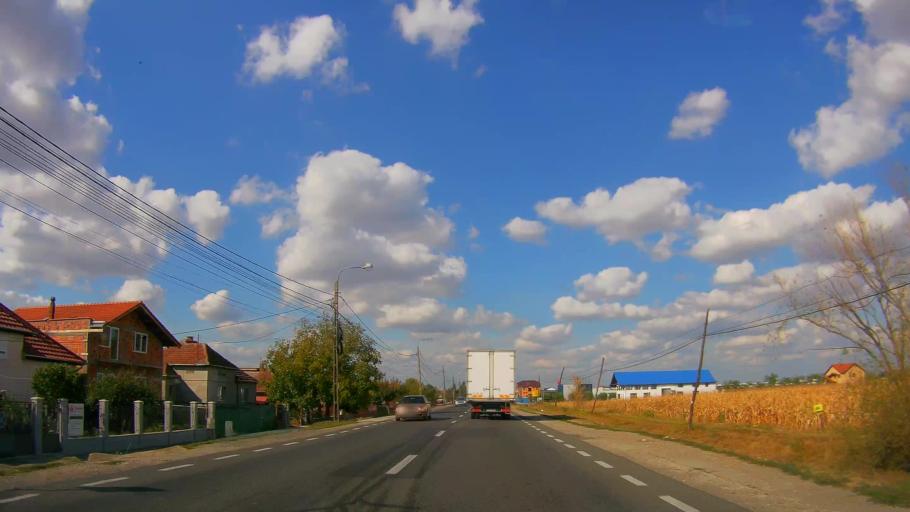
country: RO
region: Satu Mare
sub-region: Comuna Paulesti
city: Paulesti
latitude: 47.7492
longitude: 22.8832
